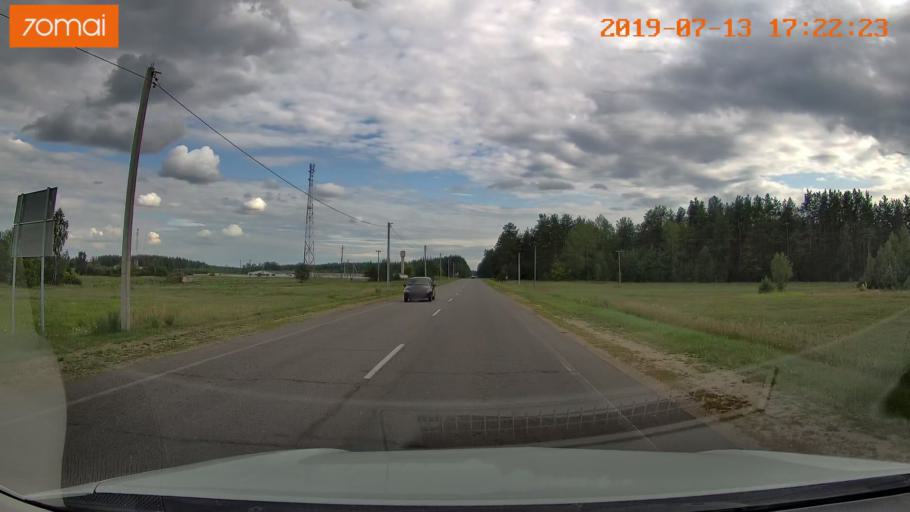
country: BY
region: Mogilev
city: Babruysk
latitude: 53.2716
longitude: 29.2343
